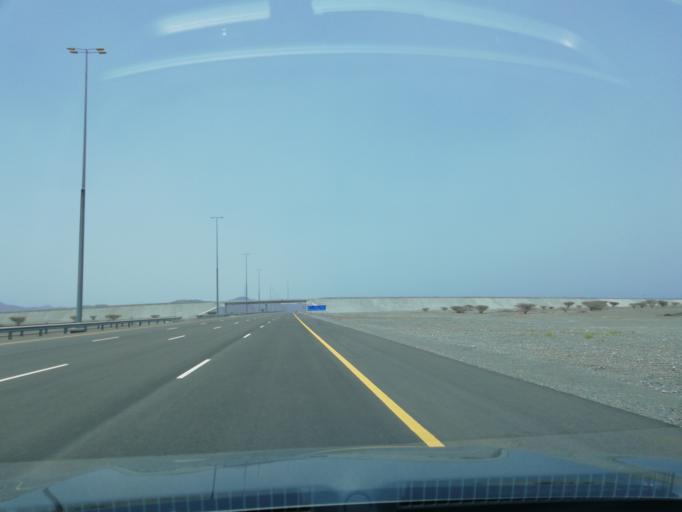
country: OM
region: Al Batinah
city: Shinas
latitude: 24.9023
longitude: 56.3545
